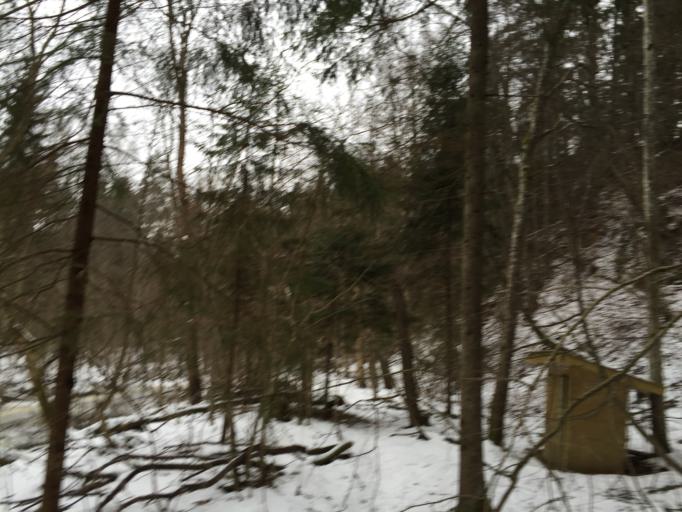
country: LV
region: Seja
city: Loja
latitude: 57.1446
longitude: 24.6817
